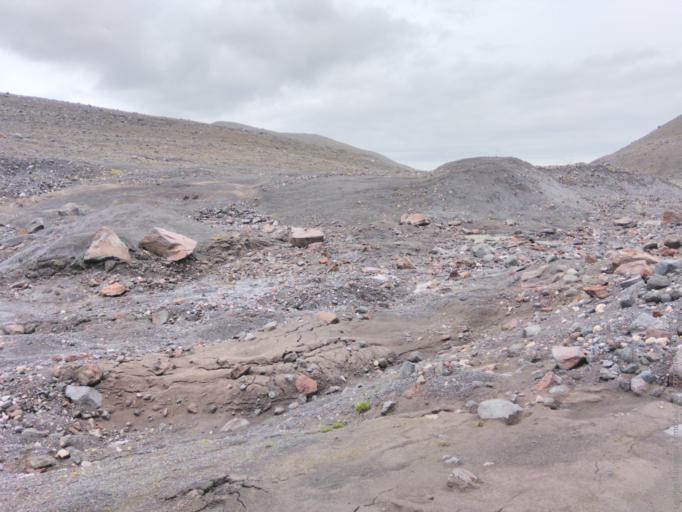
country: RU
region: Kabardino-Balkariya
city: Terskol
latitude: 43.3807
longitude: 42.5465
